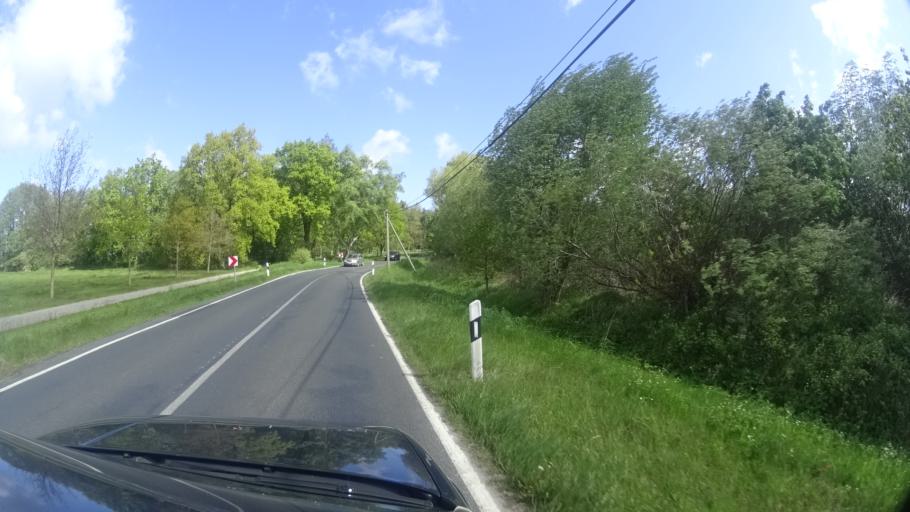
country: DE
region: Mecklenburg-Vorpommern
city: Born
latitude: 54.3510
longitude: 12.5887
